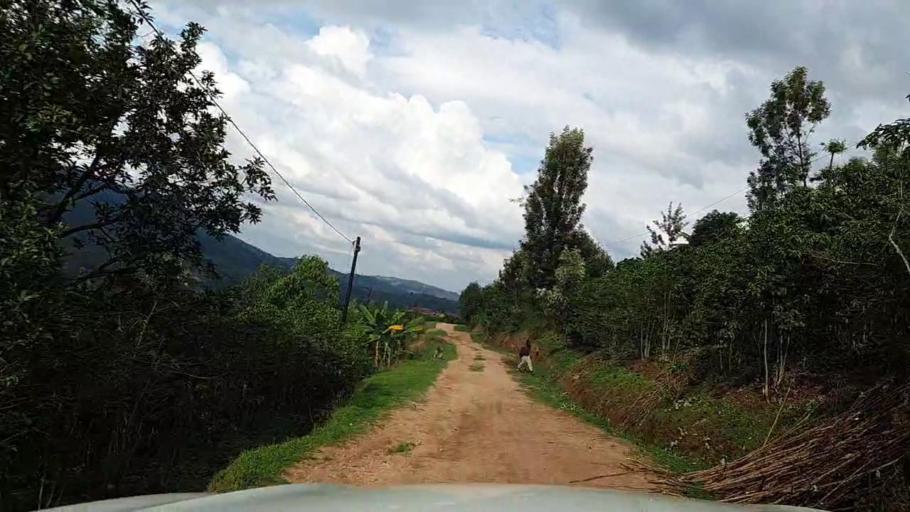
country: RW
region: Southern Province
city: Gikongoro
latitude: -2.4253
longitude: 29.6416
